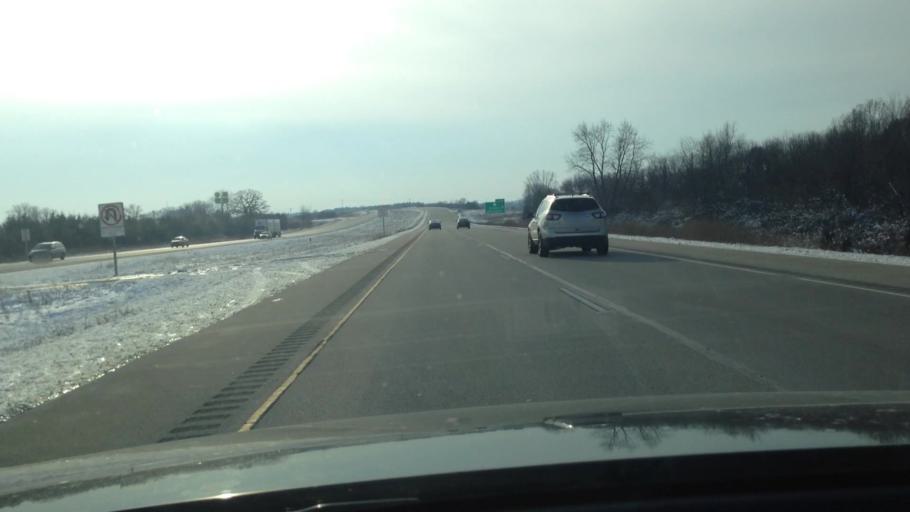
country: US
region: Wisconsin
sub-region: Walworth County
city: Elkhorn
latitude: 42.6980
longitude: -88.4952
